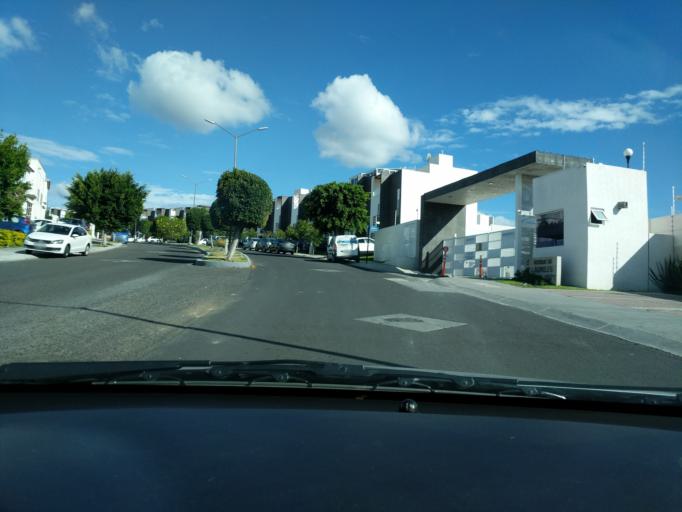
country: MX
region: Queretaro
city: La Canada
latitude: 20.5860
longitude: -100.3383
